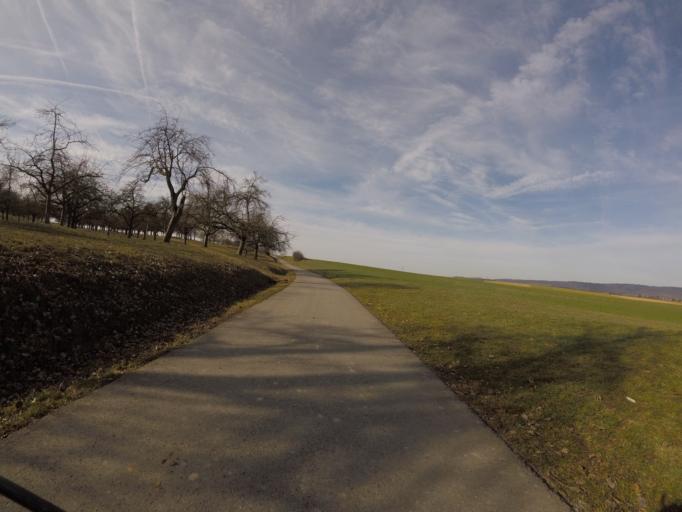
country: DE
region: Baden-Wuerttemberg
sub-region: Regierungsbezirk Stuttgart
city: Mittelschontal
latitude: 48.9529
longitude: 9.3881
